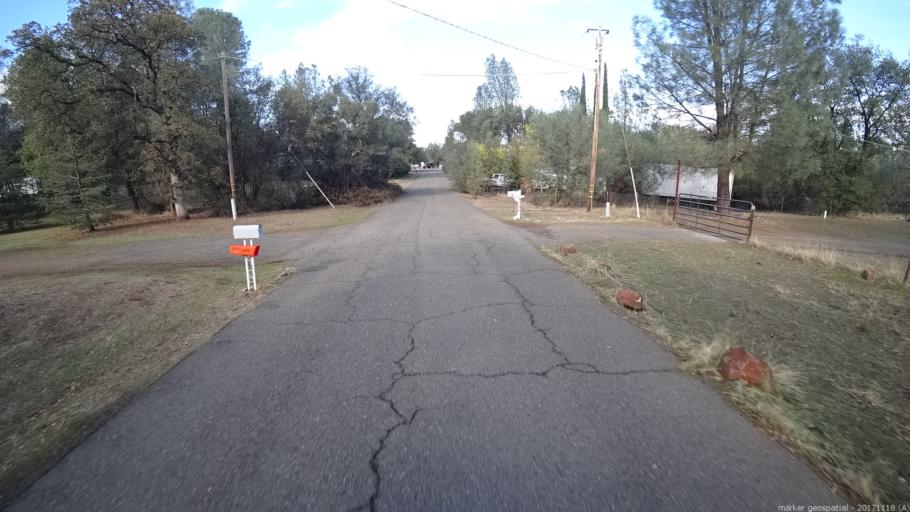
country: US
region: California
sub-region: Shasta County
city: Redding
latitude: 40.4711
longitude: -122.4131
